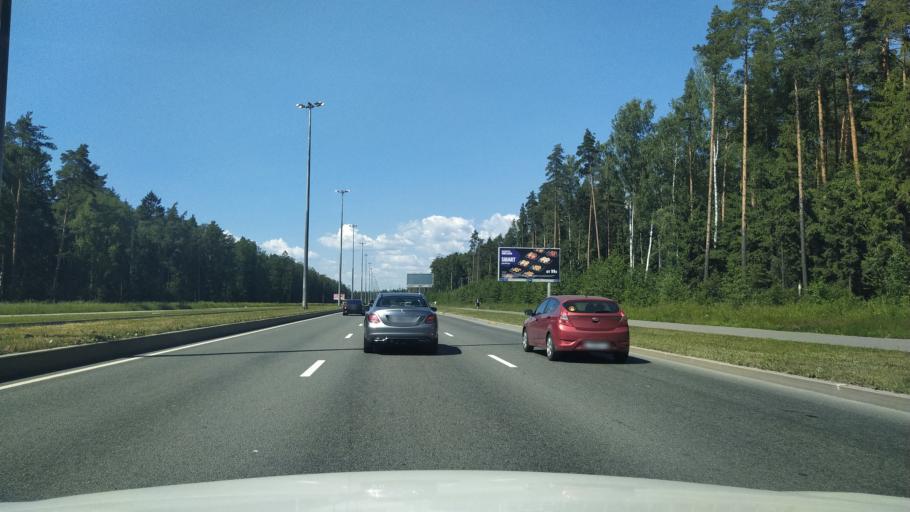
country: RU
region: Leningrad
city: Untolovo
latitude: 60.0549
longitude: 30.2248
